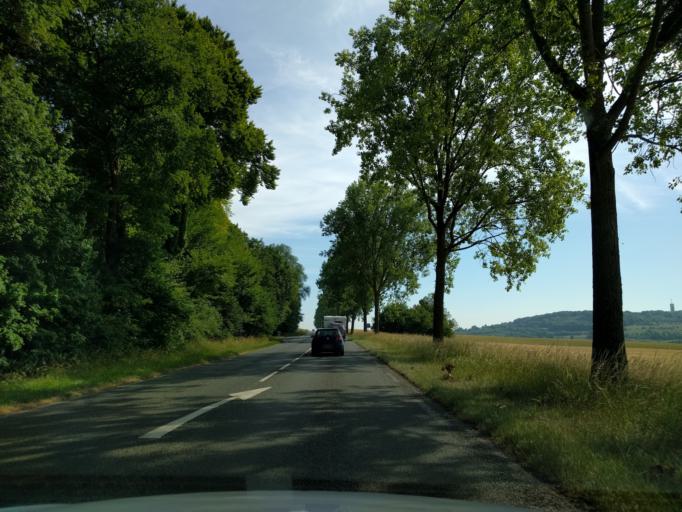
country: FR
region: Picardie
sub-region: Departement de l'Oise
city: Breteuil
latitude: 49.5929
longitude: 2.2692
